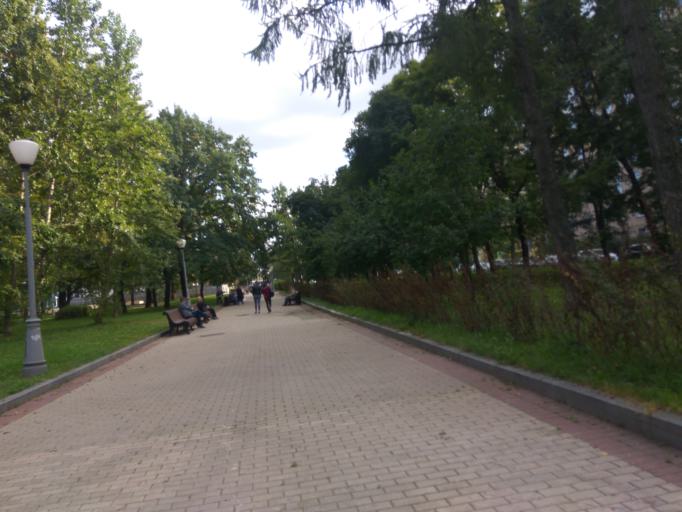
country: RU
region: Moscow
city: Vorob'yovo
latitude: 55.7395
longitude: 37.5216
